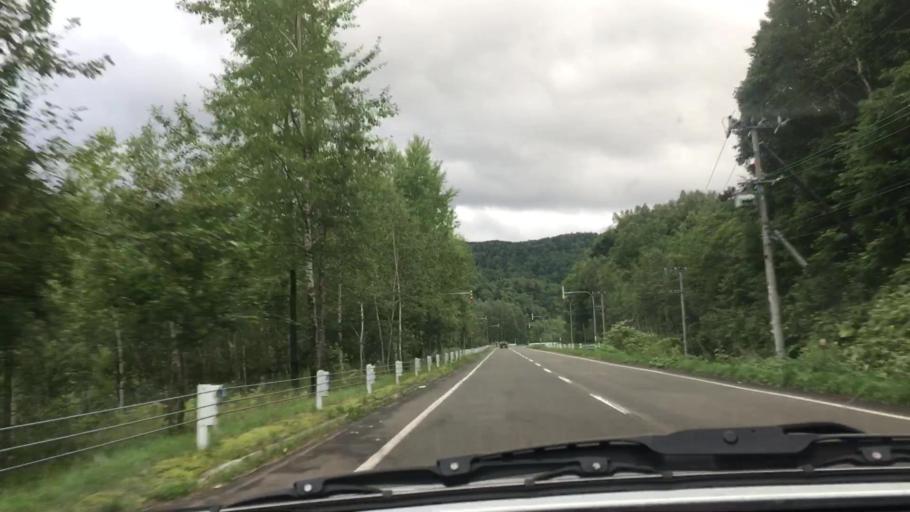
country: JP
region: Hokkaido
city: Shimo-furano
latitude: 43.0532
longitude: 142.5329
